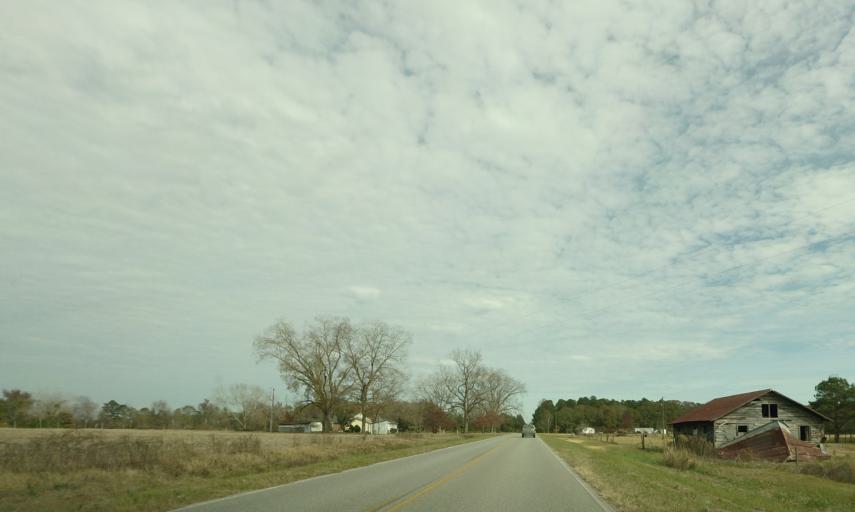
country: US
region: Georgia
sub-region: Dodge County
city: Chester
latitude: 32.4493
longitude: -83.1482
